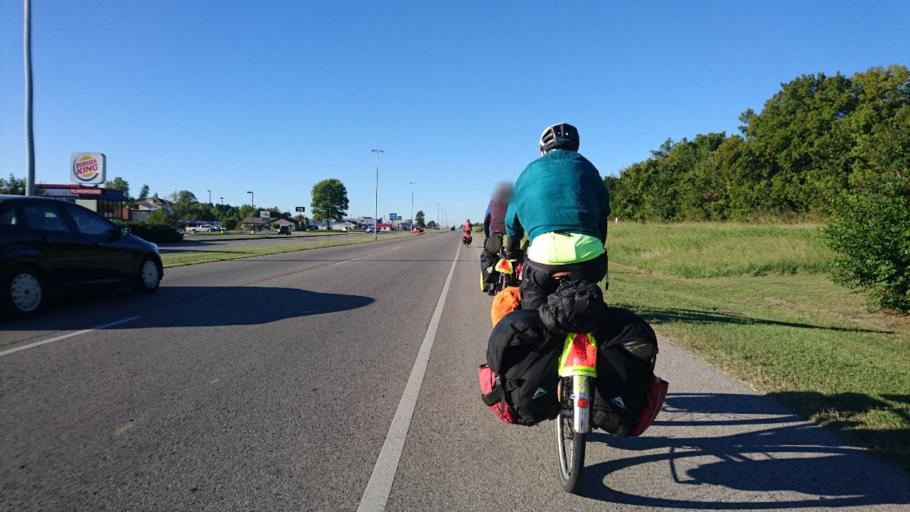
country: US
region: Oklahoma
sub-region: Rogers County
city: Claremore
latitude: 36.3009
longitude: -95.6257
